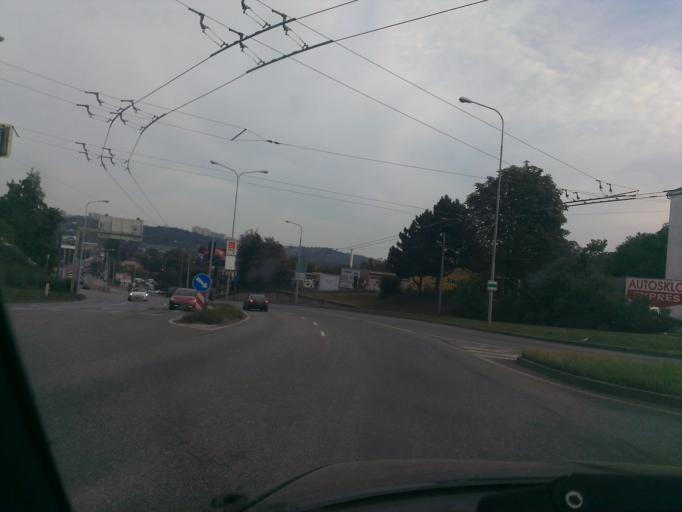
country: CZ
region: South Moravian
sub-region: Mesto Brno
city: Brno
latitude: 49.2146
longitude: 16.6337
